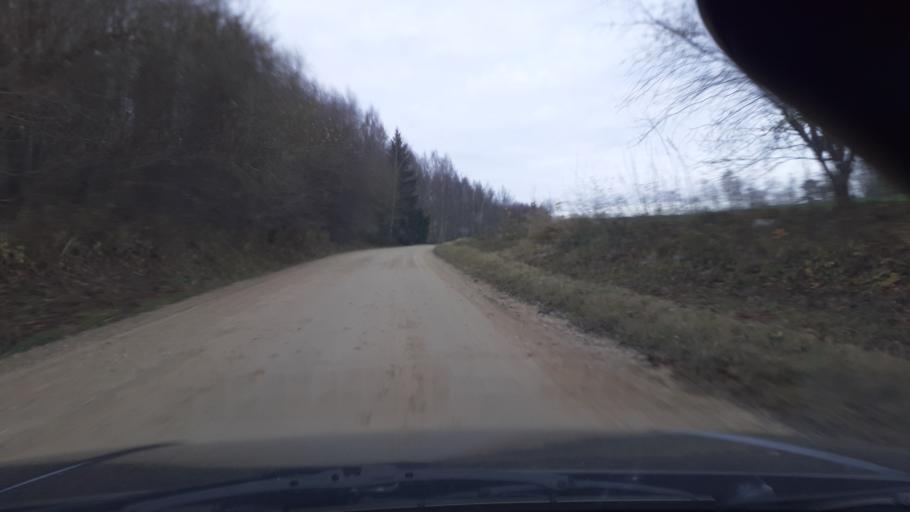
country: LV
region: Alsunga
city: Alsunga
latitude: 56.9572
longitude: 21.6499
